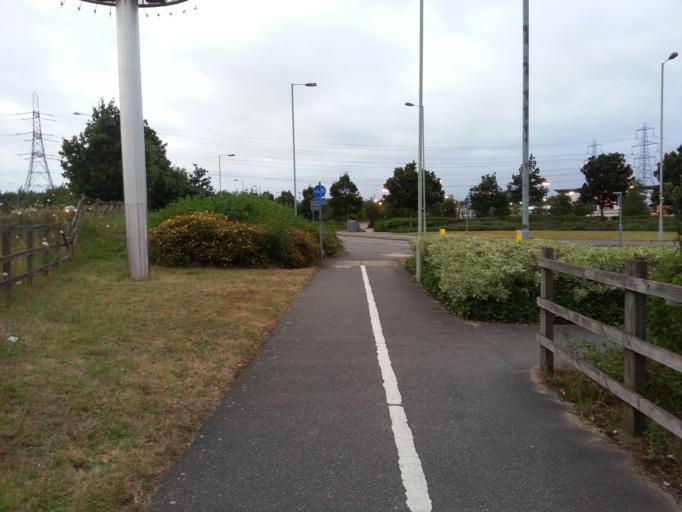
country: GB
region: England
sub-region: Suffolk
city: Bramford
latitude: 52.0845
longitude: 1.1161
